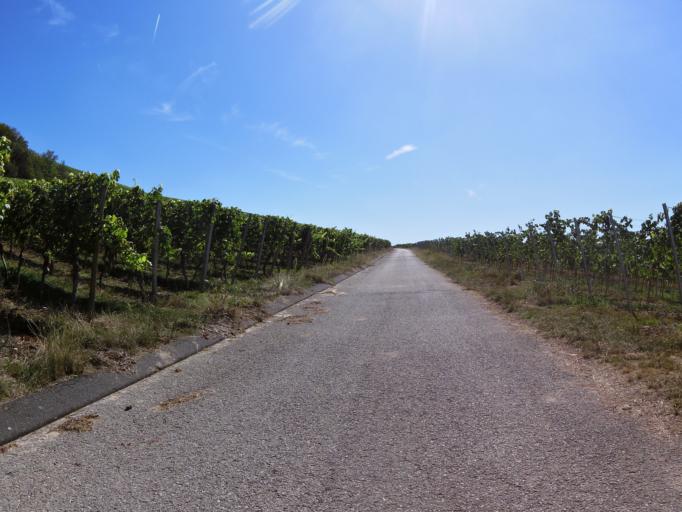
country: DE
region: Bavaria
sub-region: Regierungsbezirk Unterfranken
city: Thungersheim
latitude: 49.8737
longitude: 9.8547
